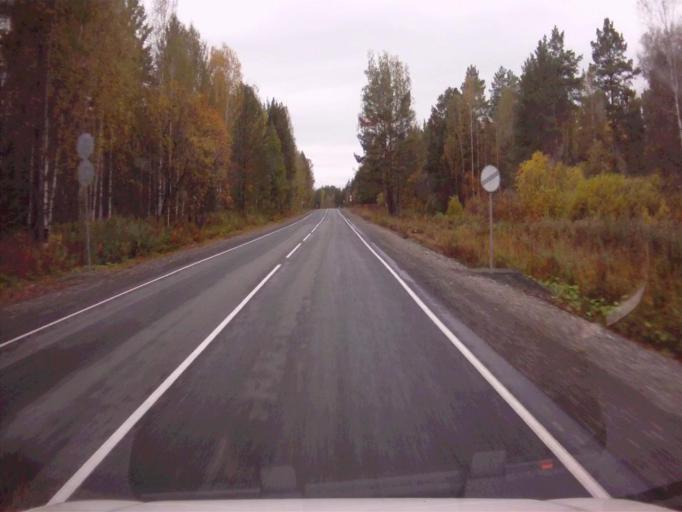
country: RU
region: Chelyabinsk
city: Nyazepetrovsk
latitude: 56.0582
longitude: 59.7335
